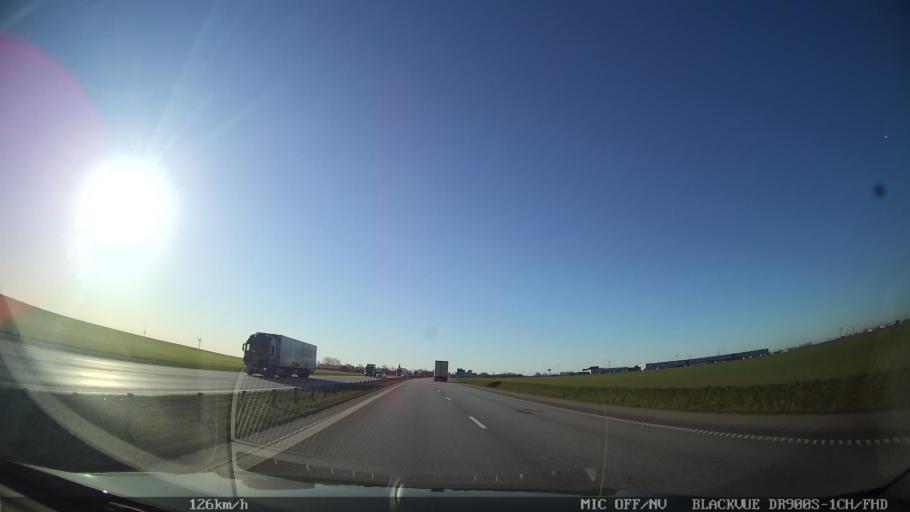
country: SE
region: Skane
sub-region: Landskrona
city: Landskrona
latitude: 55.8873
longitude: 12.8741
